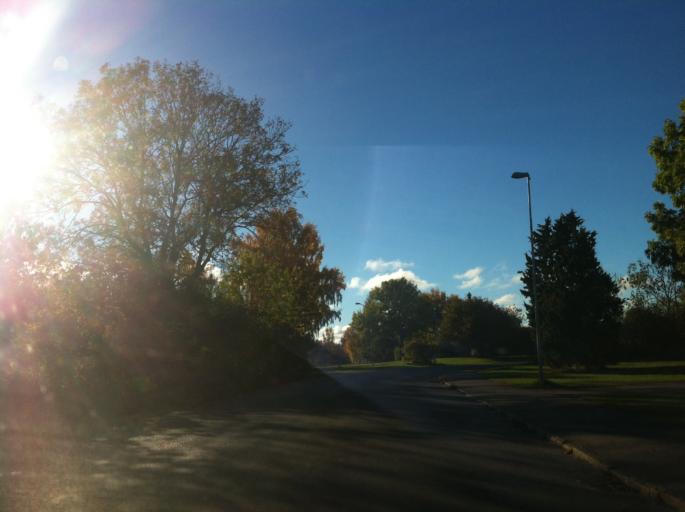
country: SE
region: Uppsala
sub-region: Osthammars Kommun
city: Oregrund
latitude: 60.3363
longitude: 18.4444
